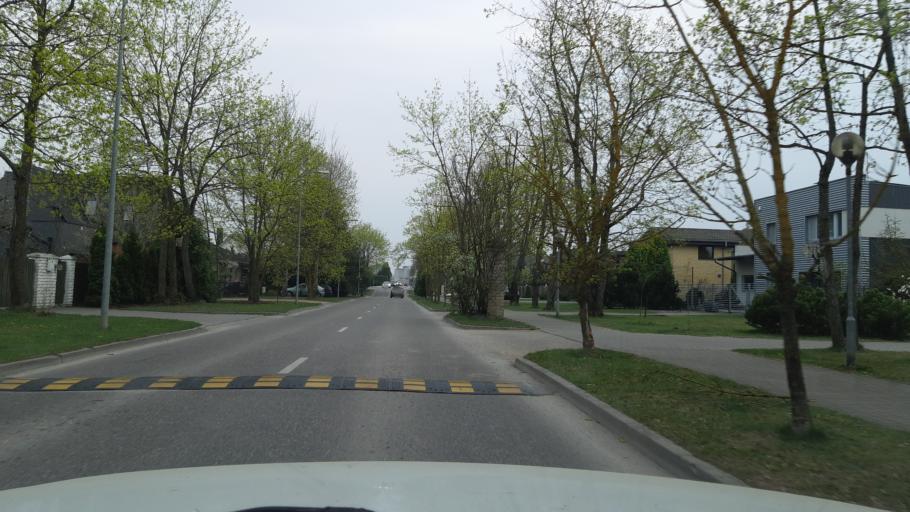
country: LT
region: Kauno apskritis
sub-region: Kaunas
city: Sargenai
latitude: 54.9433
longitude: 23.9030
